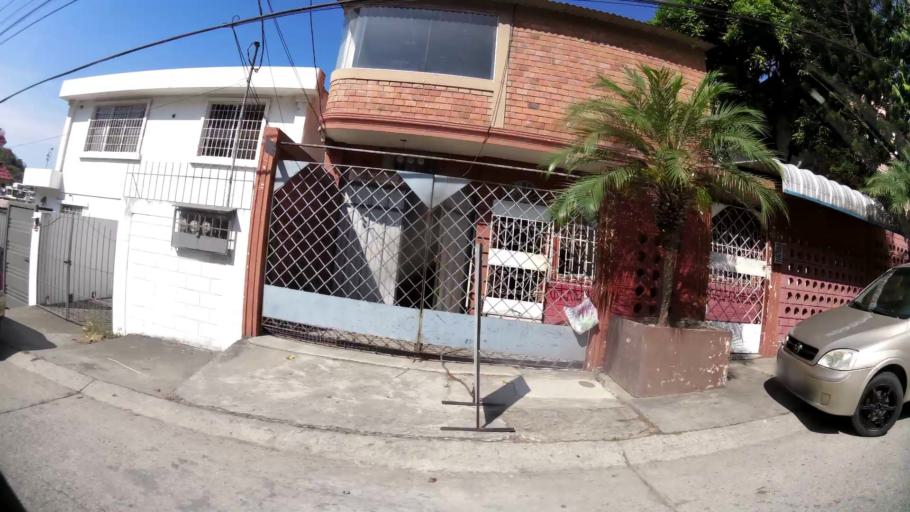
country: EC
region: Guayas
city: Guayaquil
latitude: -2.1797
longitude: -79.9113
